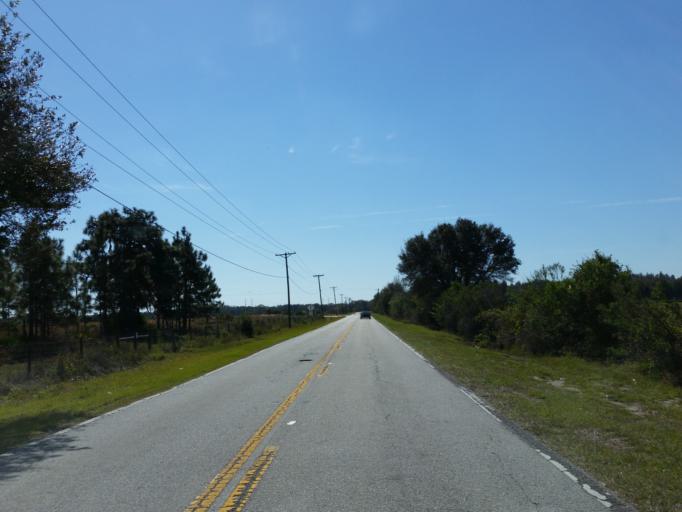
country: US
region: Florida
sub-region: Hillsborough County
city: Boyette
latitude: 27.8201
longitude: -82.2320
